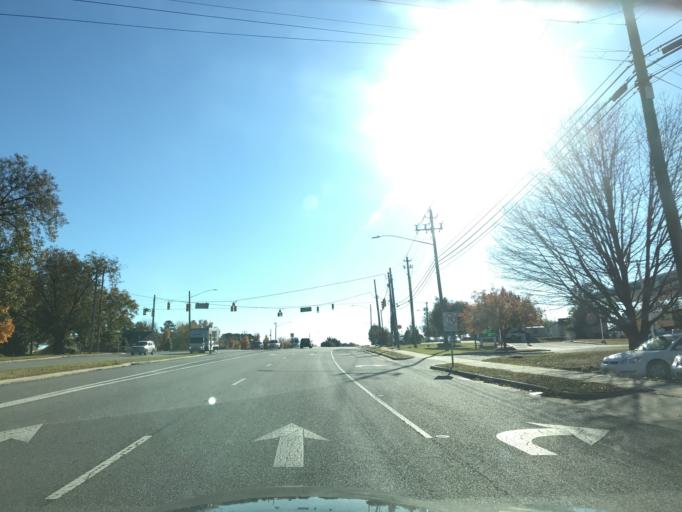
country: US
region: North Carolina
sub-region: Wake County
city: Raleigh
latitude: 35.7492
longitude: -78.6434
